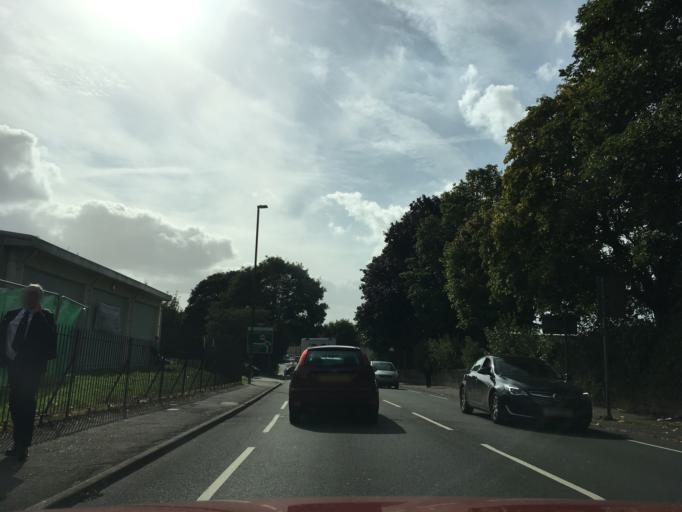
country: GB
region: England
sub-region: Gloucestershire
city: Stroud
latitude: 51.7448
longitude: -2.2373
